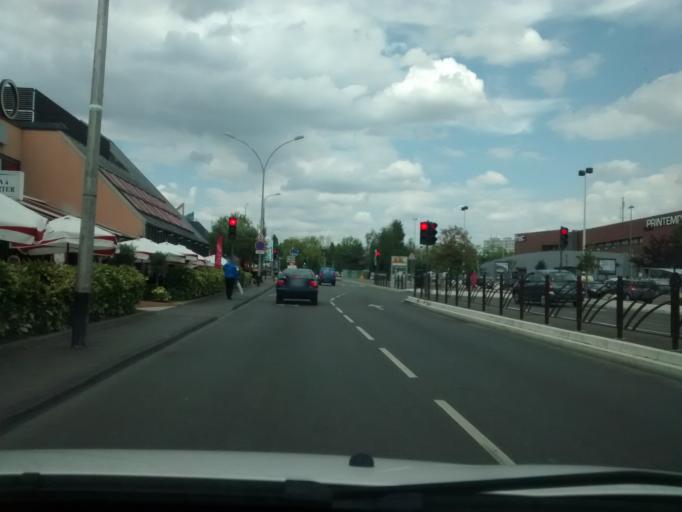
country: FR
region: Ile-de-France
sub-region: Departement de l'Essonne
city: Bievres
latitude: 48.7817
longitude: 2.2188
